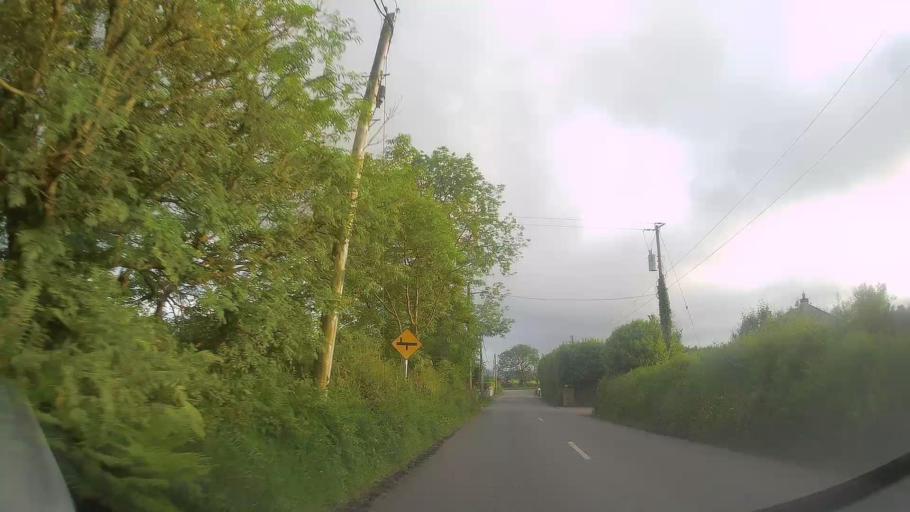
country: IE
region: Munster
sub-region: County Cork
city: Blarney
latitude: 51.9752
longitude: -8.5545
